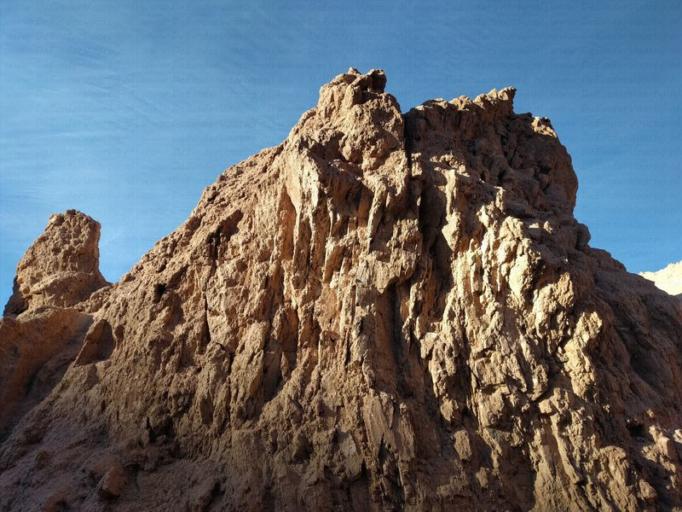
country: CL
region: Antofagasta
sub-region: Provincia de El Loa
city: San Pedro de Atacama
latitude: -22.9020
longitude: -68.2260
